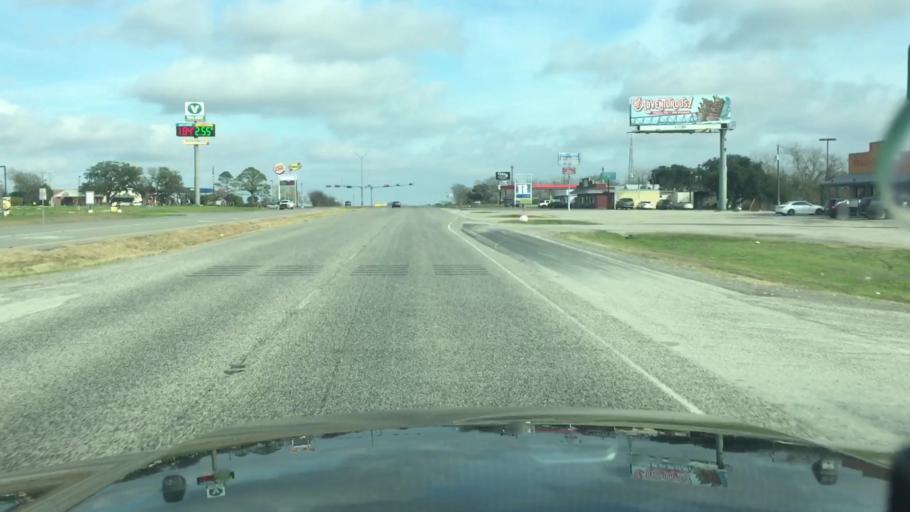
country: US
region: Texas
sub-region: Washington County
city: Brenham
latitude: 30.1348
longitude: -96.2597
